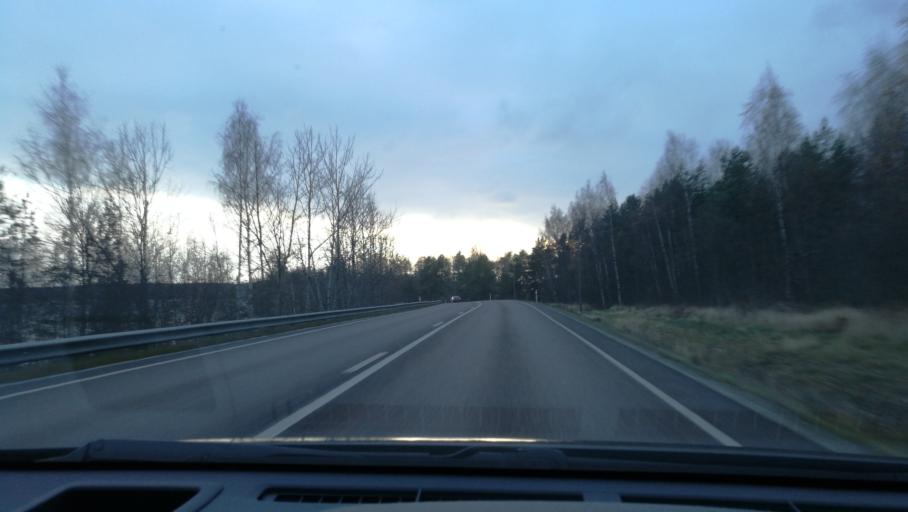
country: SE
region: Vaestmanland
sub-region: Kungsors Kommun
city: Kungsoer
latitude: 59.2538
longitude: 16.1109
